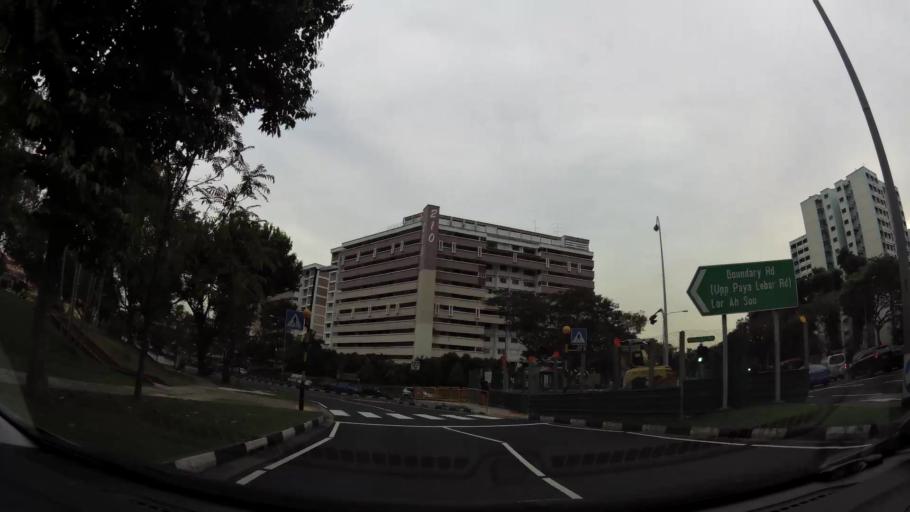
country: SG
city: Singapore
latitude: 1.3559
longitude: 103.8738
